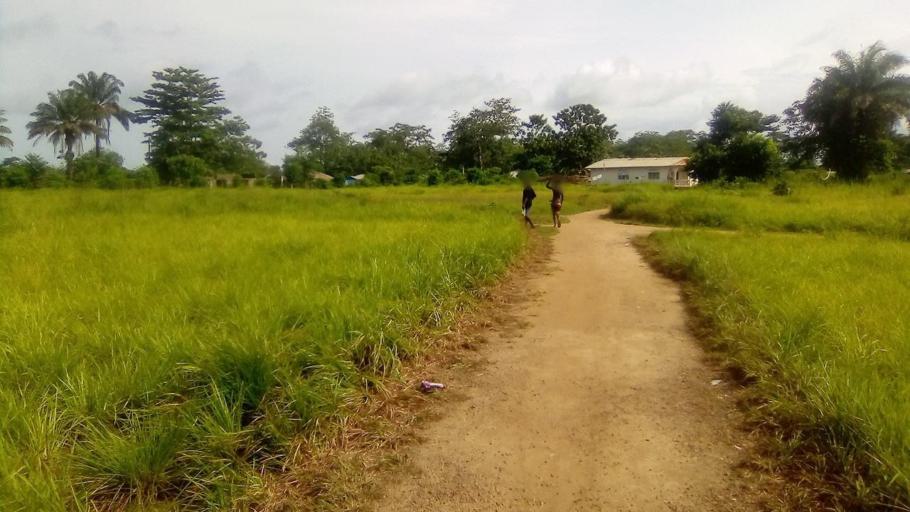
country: SL
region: Southern Province
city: Pujehun
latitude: 7.3619
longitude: -11.7292
